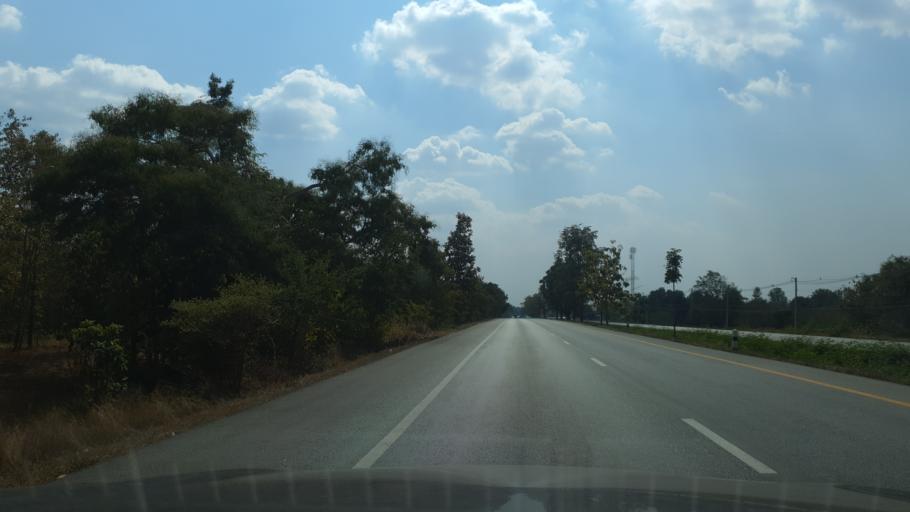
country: TH
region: Tak
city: Sam Ngao
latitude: 17.2937
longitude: 99.1427
